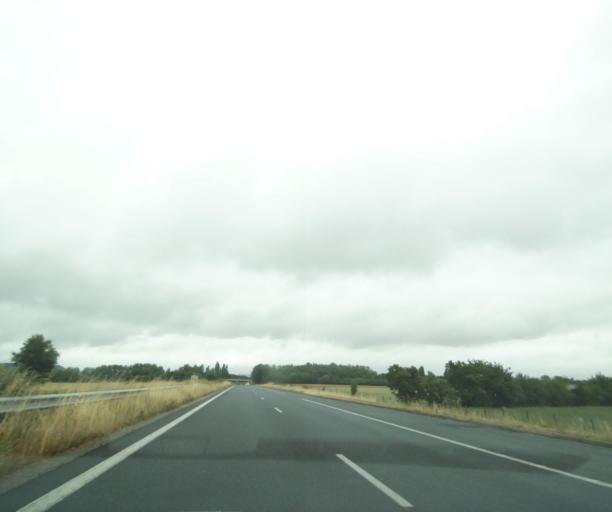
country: FR
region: Midi-Pyrenees
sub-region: Departement du Tarn
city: Marssac-sur-Tarn
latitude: 43.8987
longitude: 2.0317
